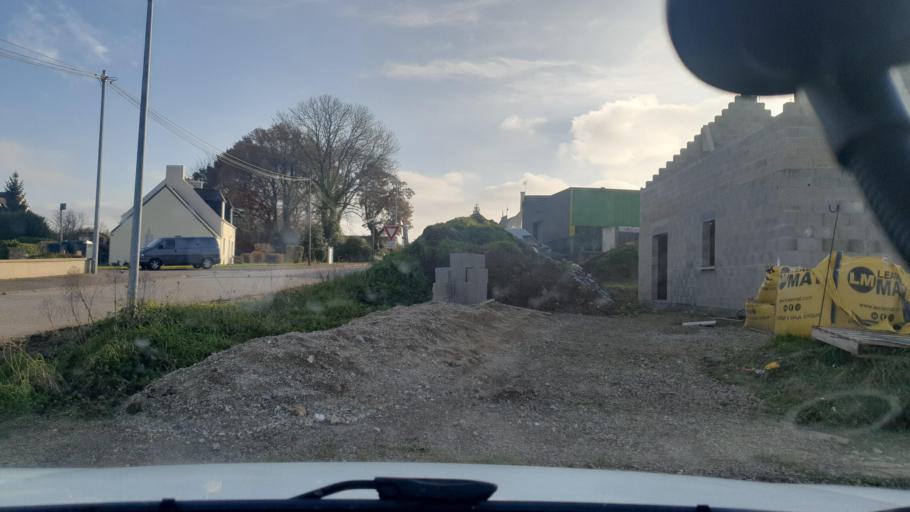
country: FR
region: Brittany
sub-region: Departement du Finistere
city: Briec
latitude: 48.1027
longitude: -4.0094
